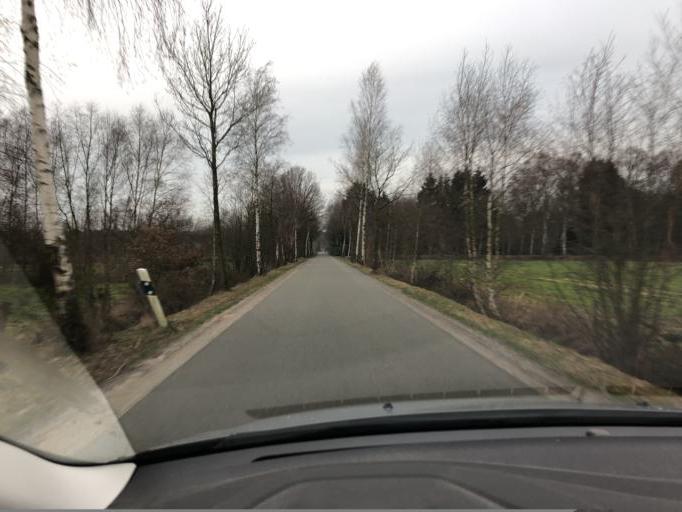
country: DE
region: Lower Saxony
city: Bad Zwischenahn
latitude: 53.1659
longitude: 8.0458
